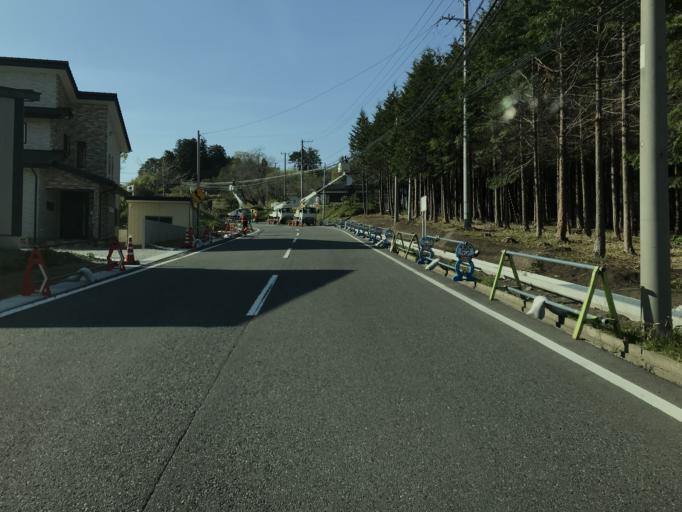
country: JP
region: Fukushima
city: Funehikimachi-funehiki
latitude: 37.5056
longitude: 140.7627
